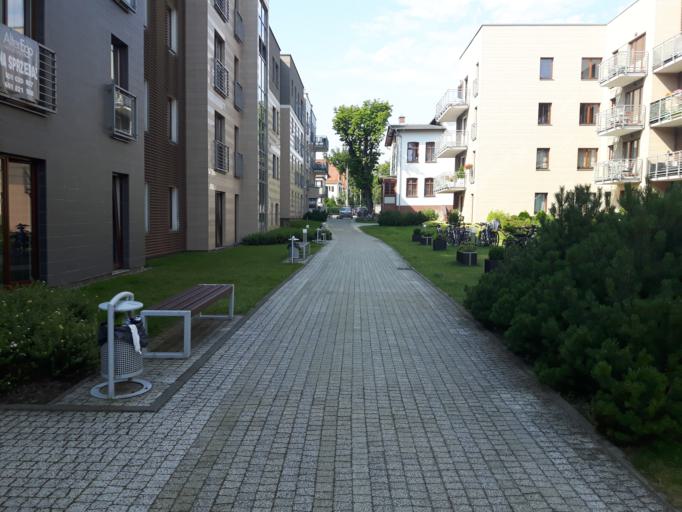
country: PL
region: Pomeranian Voivodeship
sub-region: Sopot
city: Sopot
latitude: 54.4339
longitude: 18.5723
